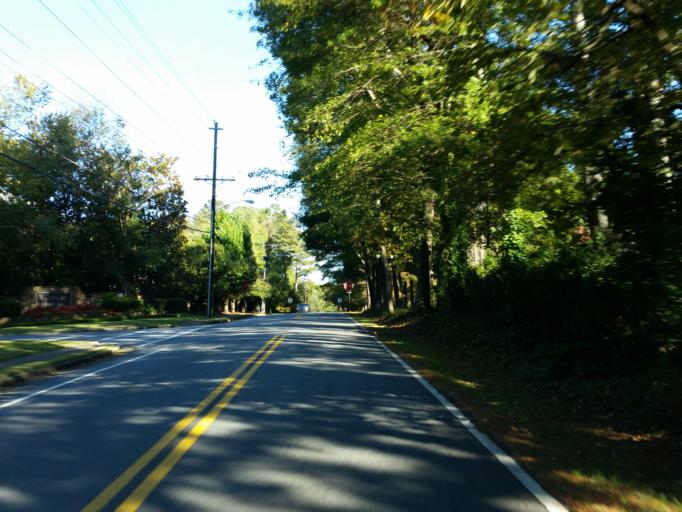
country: US
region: Georgia
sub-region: Fulton County
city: Roswell
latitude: 33.9930
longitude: -84.3978
